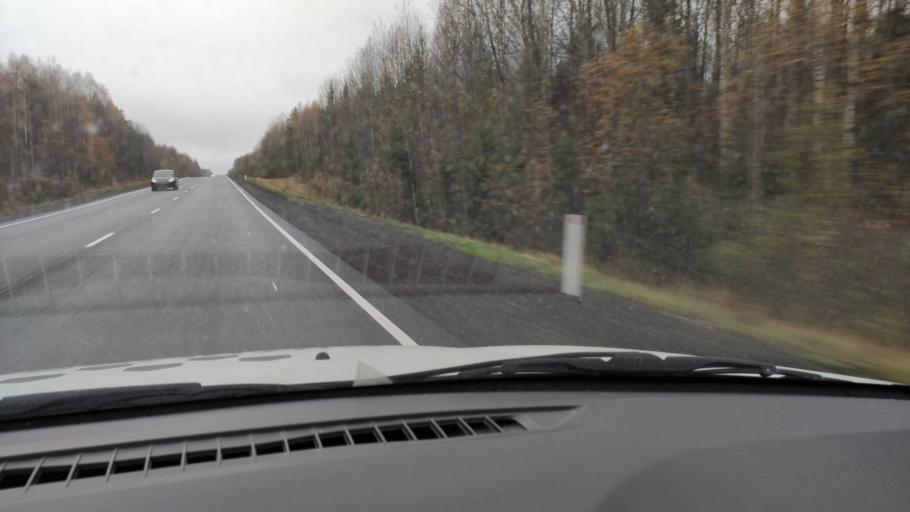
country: RU
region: Kirov
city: Chernaya Kholunitsa
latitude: 58.8818
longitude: 51.4303
